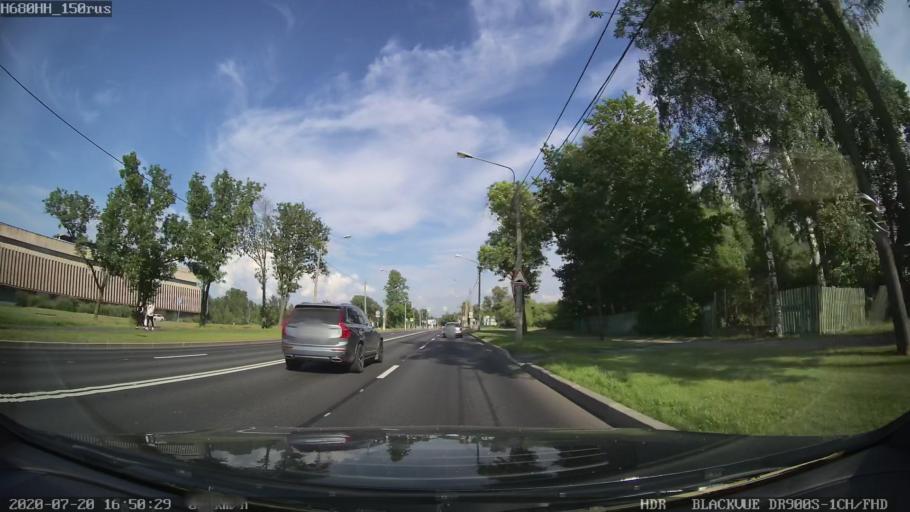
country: RU
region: St.-Petersburg
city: Strel'na
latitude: 59.8518
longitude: 30.0781
